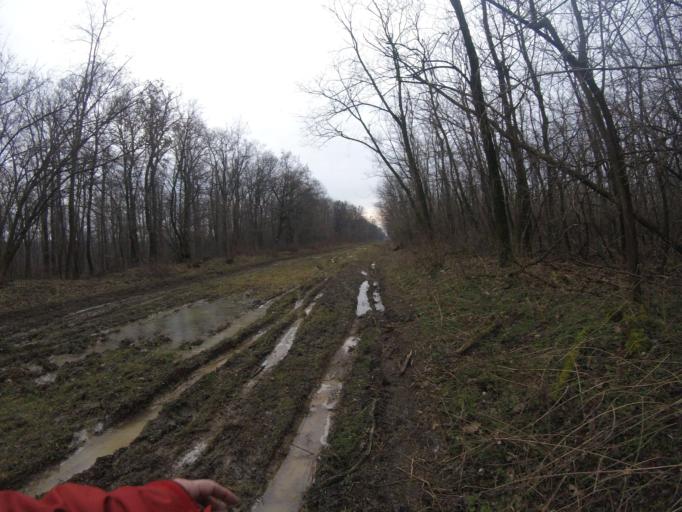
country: HU
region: Baranya
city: Pecsvarad
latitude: 46.1340
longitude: 18.5236
